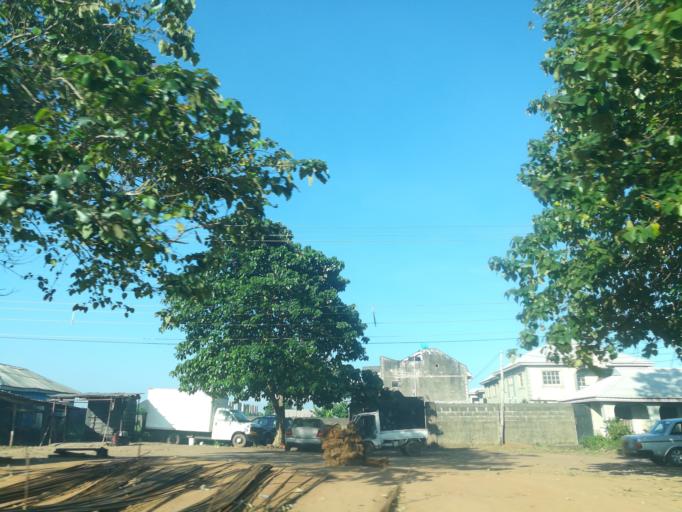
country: NG
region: Lagos
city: Ikorodu
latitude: 6.5581
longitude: 3.5381
